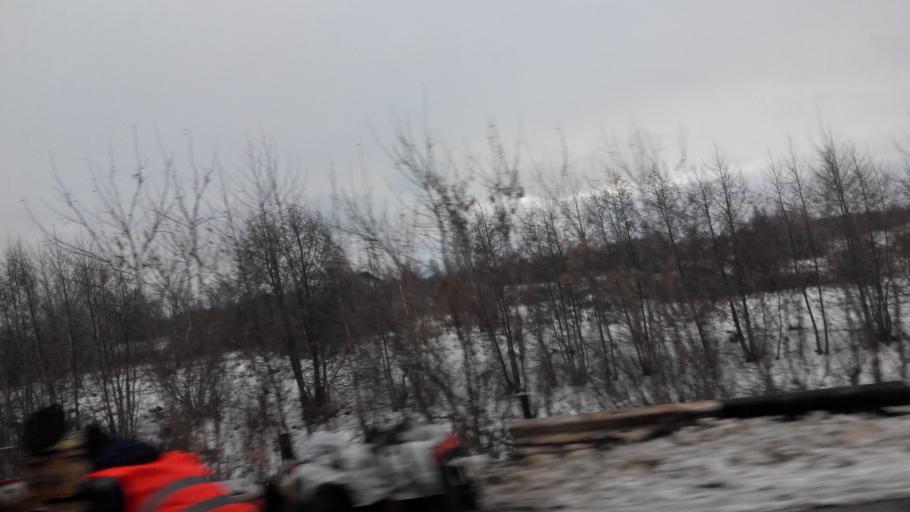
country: RU
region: Tula
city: Podlesnyy
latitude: 53.9706
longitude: 38.2508
